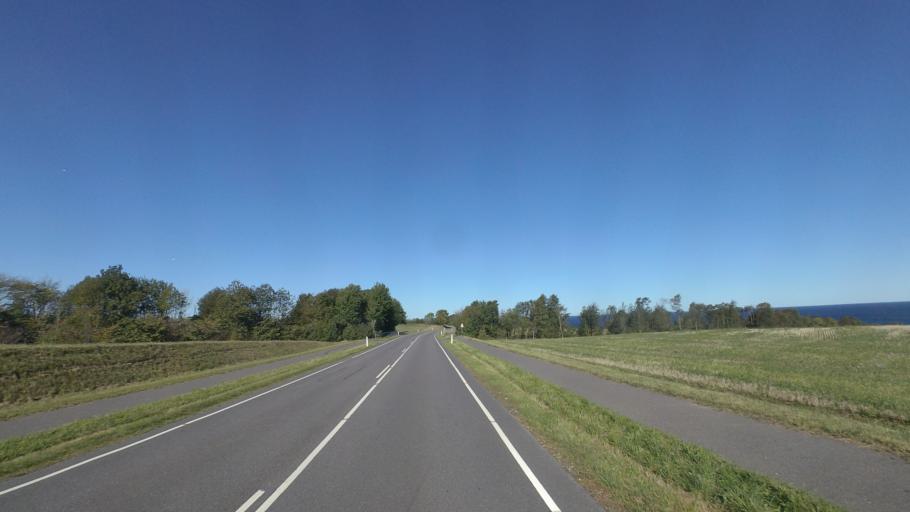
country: DK
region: Capital Region
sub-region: Bornholm Kommune
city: Nexo
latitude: 55.1670
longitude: 15.0321
